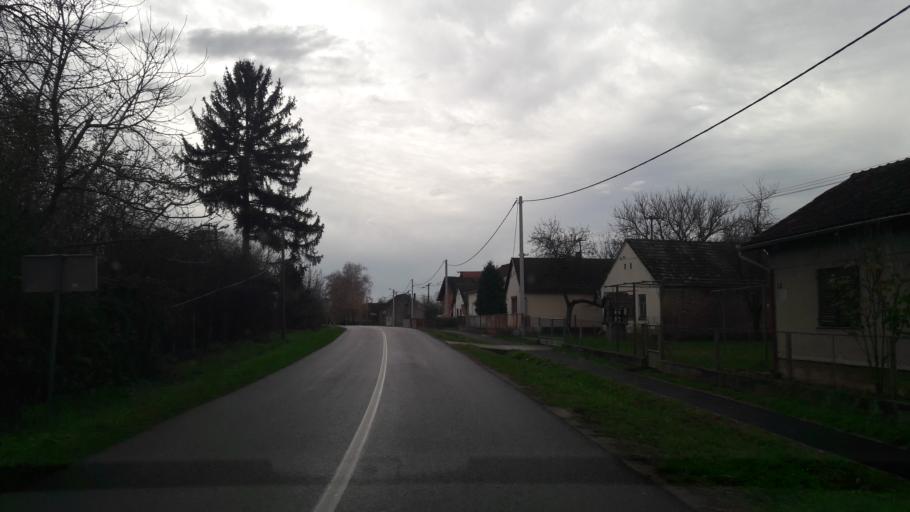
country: HR
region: Osjecko-Baranjska
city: Martin
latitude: 45.5340
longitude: 18.0608
